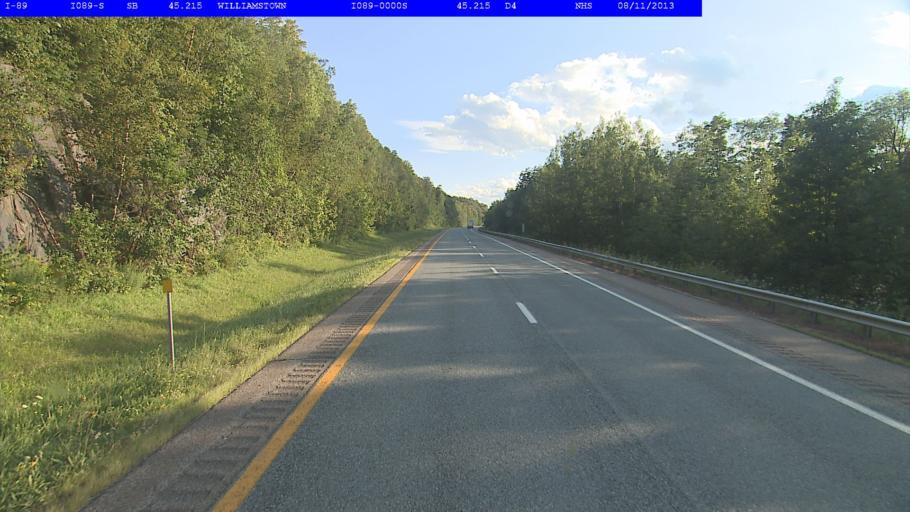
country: US
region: Vermont
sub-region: Orange County
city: Williamstown
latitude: 44.1459
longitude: -72.5942
